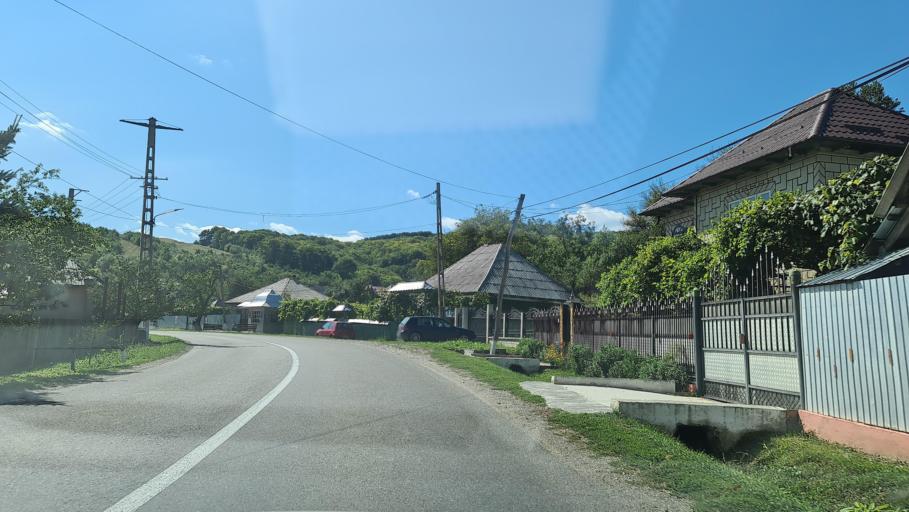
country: RO
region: Bacau
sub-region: Comuna Balcani
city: Ludasi
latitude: 46.6207
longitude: 26.5787
